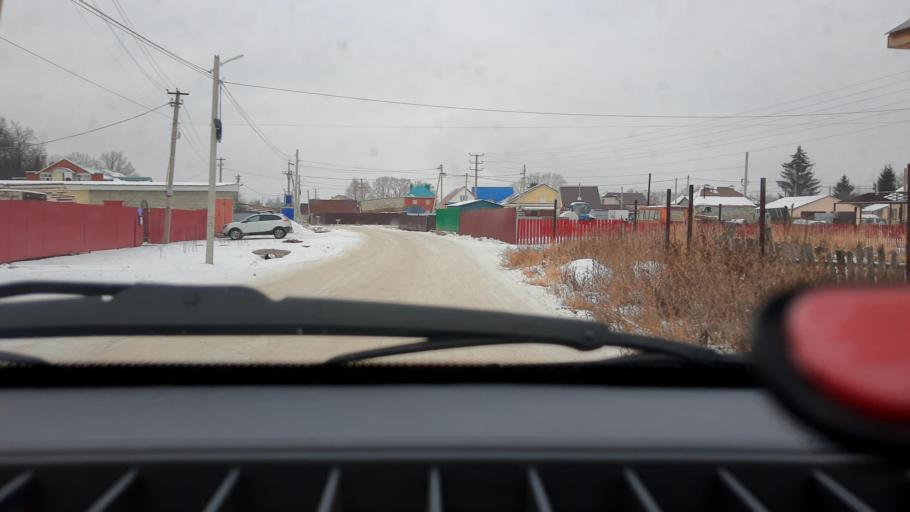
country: RU
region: Bashkortostan
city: Mikhaylovka
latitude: 54.7763
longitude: 55.8217
